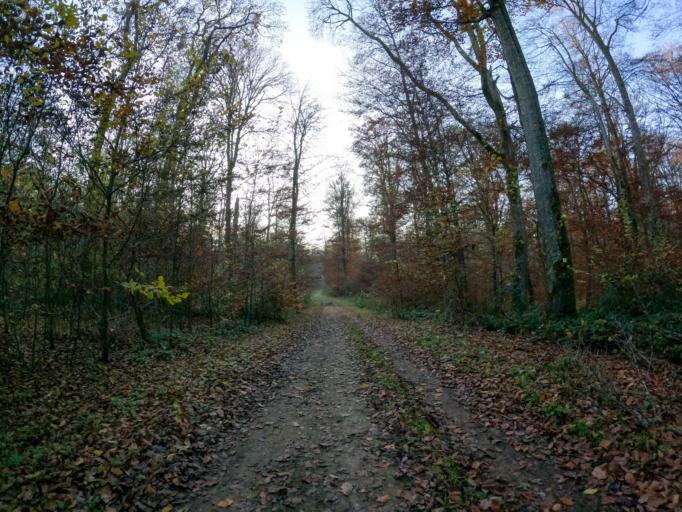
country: LU
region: Luxembourg
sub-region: Canton de Capellen
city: Dippach
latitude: 49.5990
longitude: 5.9996
